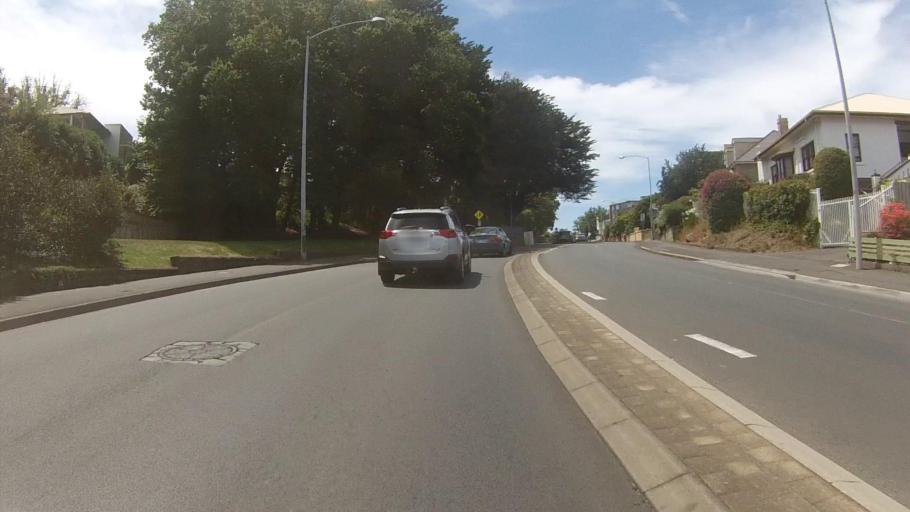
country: AU
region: Tasmania
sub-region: Hobart
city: Sandy Bay
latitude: -42.8918
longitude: 147.3265
